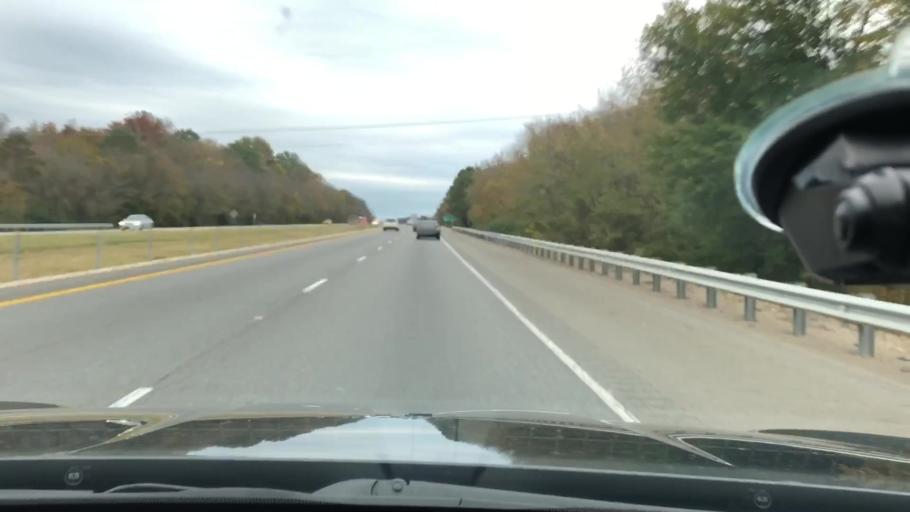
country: US
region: Arkansas
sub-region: Hot Spring County
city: Malvern
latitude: 34.3416
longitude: -92.9084
